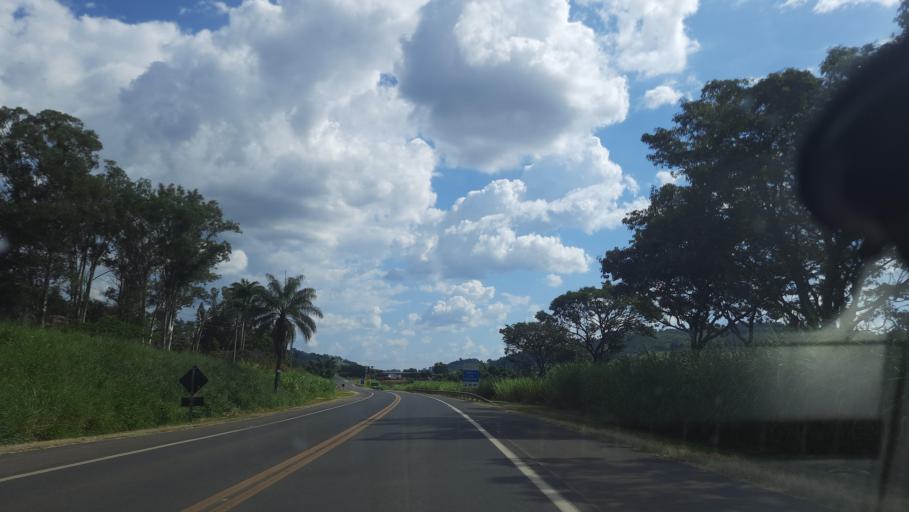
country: BR
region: Sao Paulo
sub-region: Sao Jose Do Rio Pardo
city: Sao Jose do Rio Pardo
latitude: -21.6319
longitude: -46.9020
